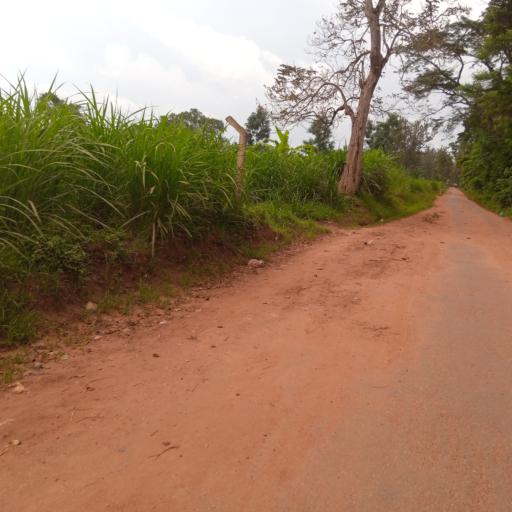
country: UG
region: Eastern Region
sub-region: Mbale District
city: Mbale
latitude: 1.0901
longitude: 34.1855
